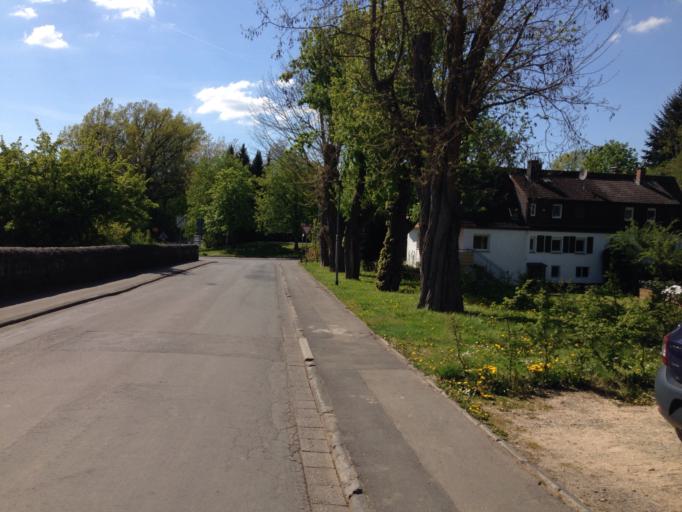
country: DE
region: Hesse
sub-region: Regierungsbezirk Giessen
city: Laubach
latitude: 50.5463
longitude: 8.9888
